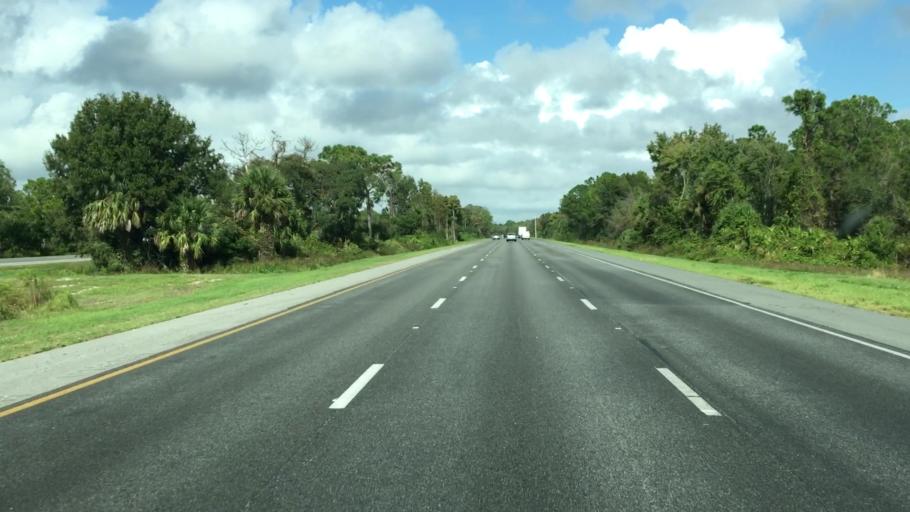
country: US
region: Florida
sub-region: Volusia County
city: Glencoe
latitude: 29.0557
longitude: -81.0075
